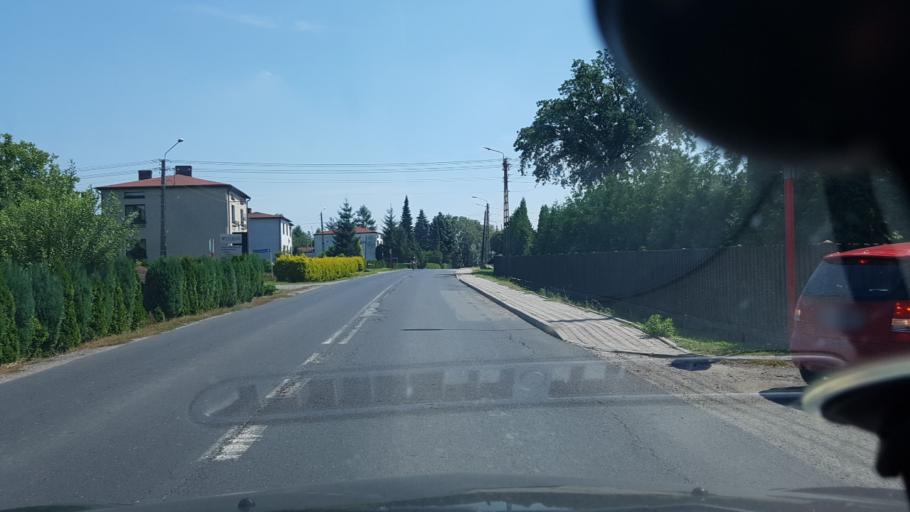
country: PL
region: Silesian Voivodeship
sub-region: Powiat wodzislawski
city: Marklowice
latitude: 50.0176
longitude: 18.5311
